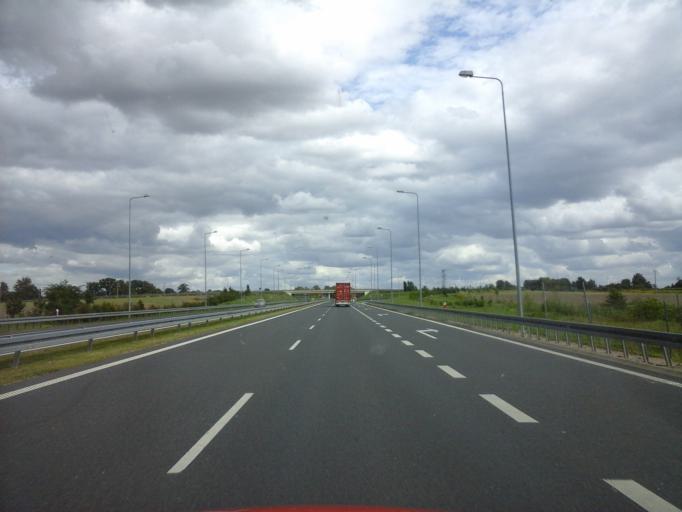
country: PL
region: West Pomeranian Voivodeship
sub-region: Powiat stargardzki
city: Stargard Szczecinski
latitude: 53.3135
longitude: 15.0881
